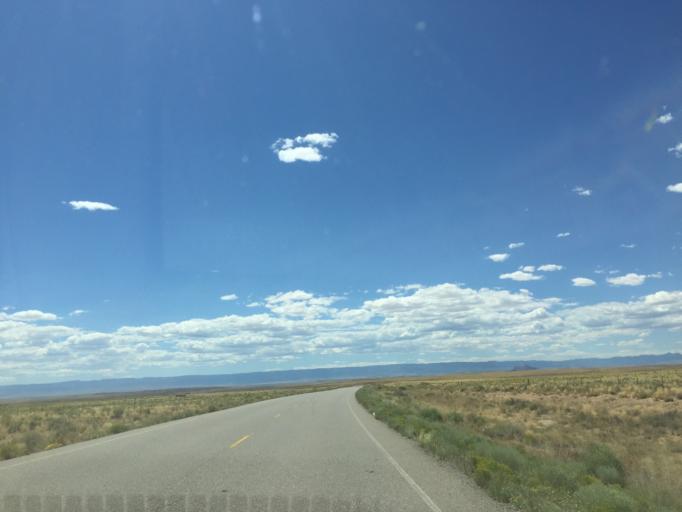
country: US
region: New Mexico
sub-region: San Juan County
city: Upper Fruitland
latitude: 36.3952
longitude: -108.4687
